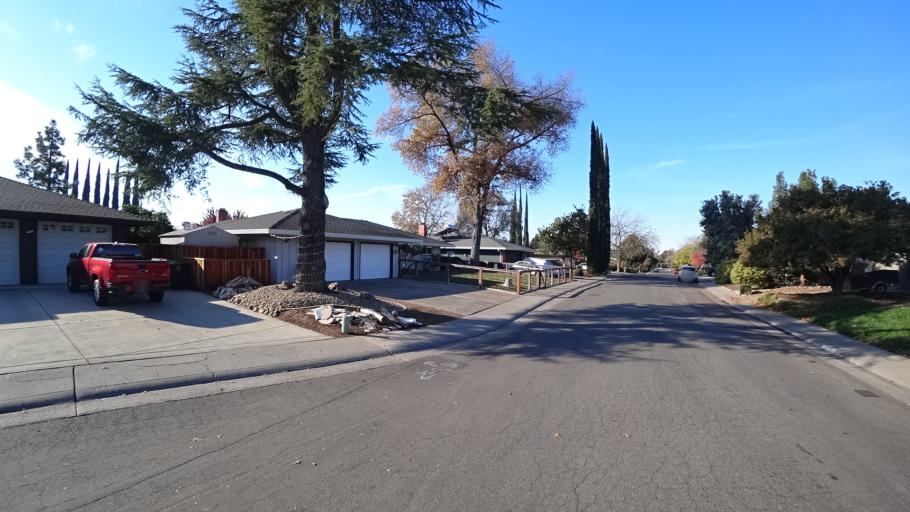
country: US
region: California
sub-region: Sacramento County
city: Citrus Heights
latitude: 38.6800
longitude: -121.3009
